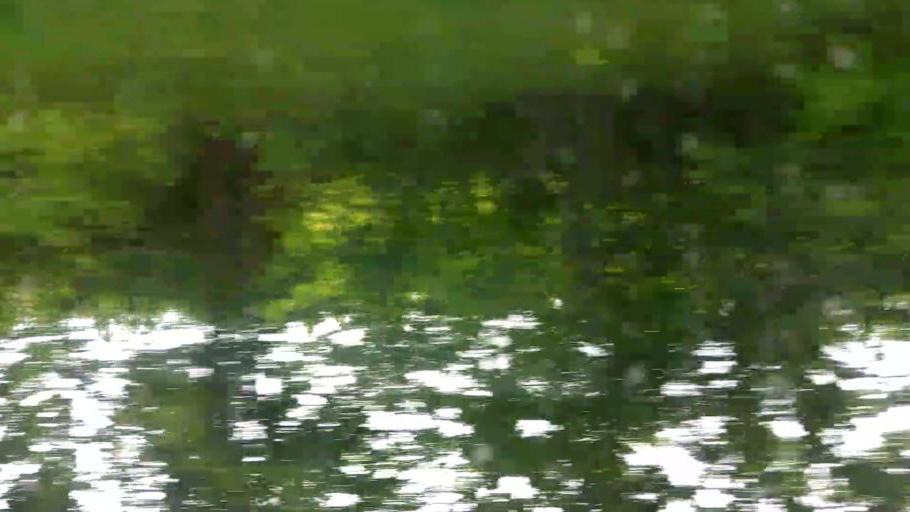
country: RU
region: Moskovskaya
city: Ozherel'ye
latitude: 54.8449
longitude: 38.2683
